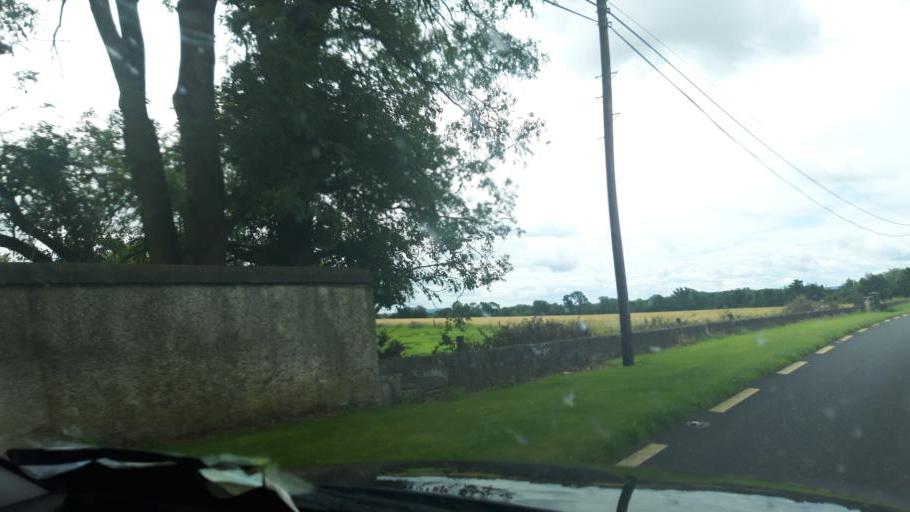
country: IE
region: Leinster
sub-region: Kilkenny
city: Callan
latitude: 52.5826
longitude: -7.3152
